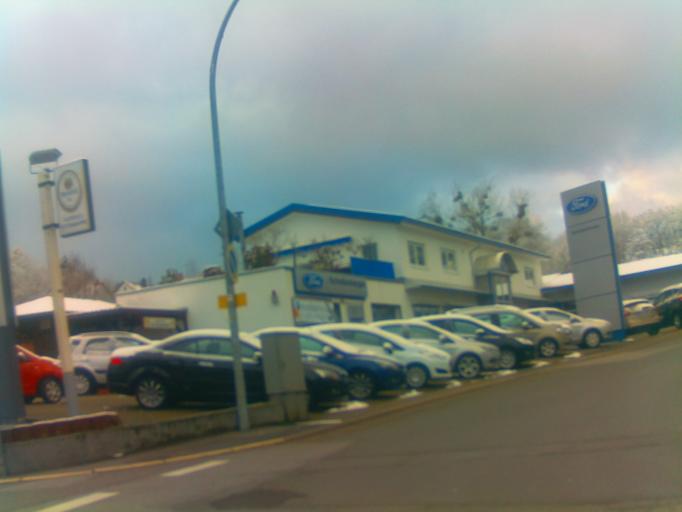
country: DE
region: Baden-Wuerttemberg
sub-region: Karlsruhe Region
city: Wilhelmsfeld
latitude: 49.5103
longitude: 8.7258
